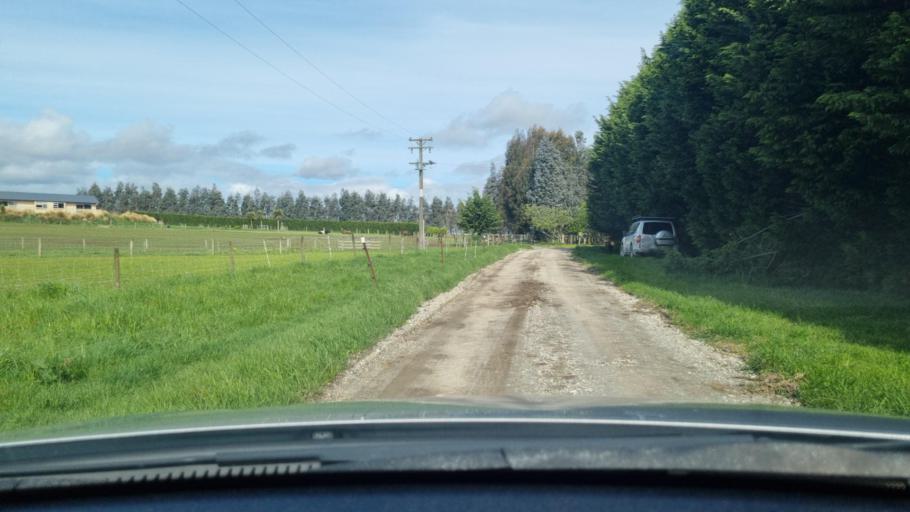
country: NZ
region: Southland
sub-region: Invercargill City
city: Invercargill
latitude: -46.4539
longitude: 168.3789
